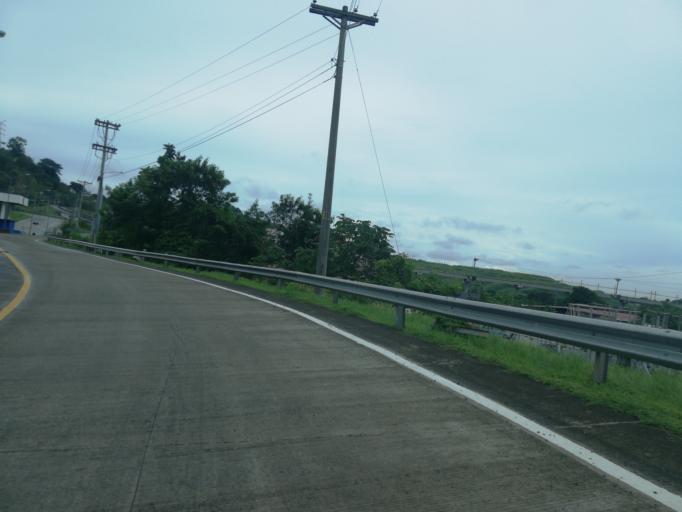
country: PA
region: Panama
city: Las Cumbres
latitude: 9.0569
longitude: -79.5120
